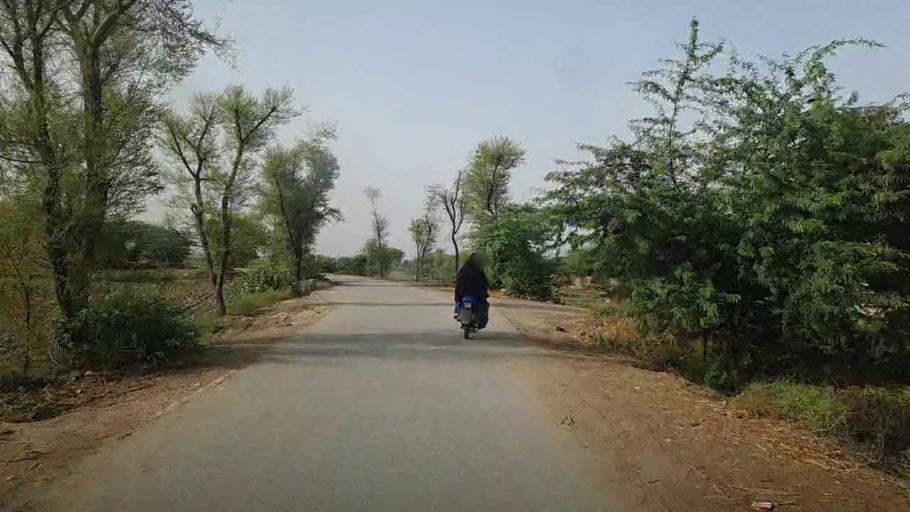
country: PK
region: Sindh
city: Khairpur Nathan Shah
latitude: 27.1119
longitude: 67.7885
